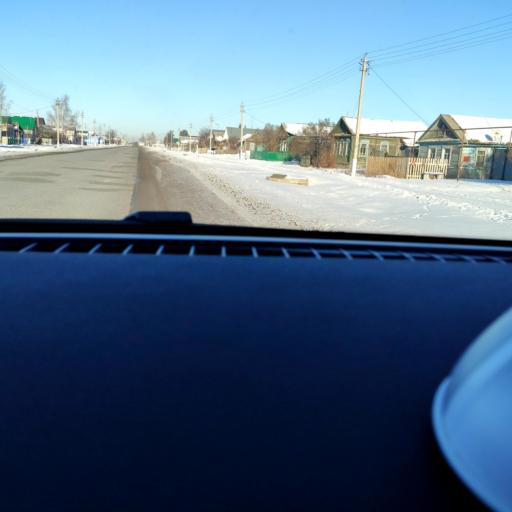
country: RU
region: Samara
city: Spiridonovka
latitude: 53.1026
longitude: 50.6463
